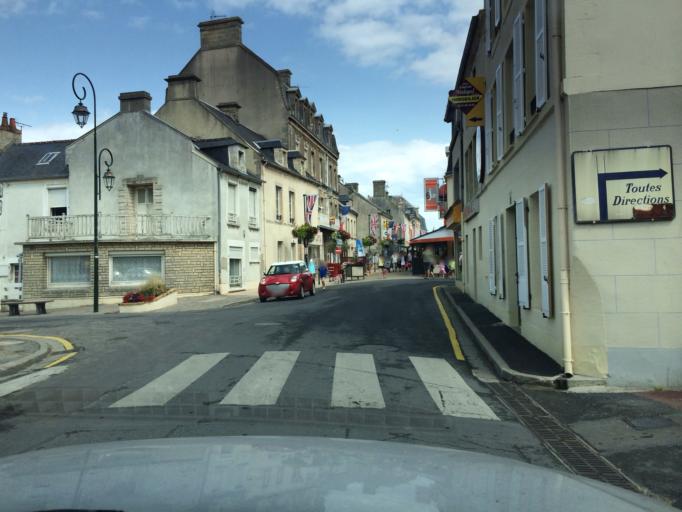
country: FR
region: Lower Normandy
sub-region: Departement du Calvados
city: Saint-Vigor-le-Grand
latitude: 49.3399
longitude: -0.6241
